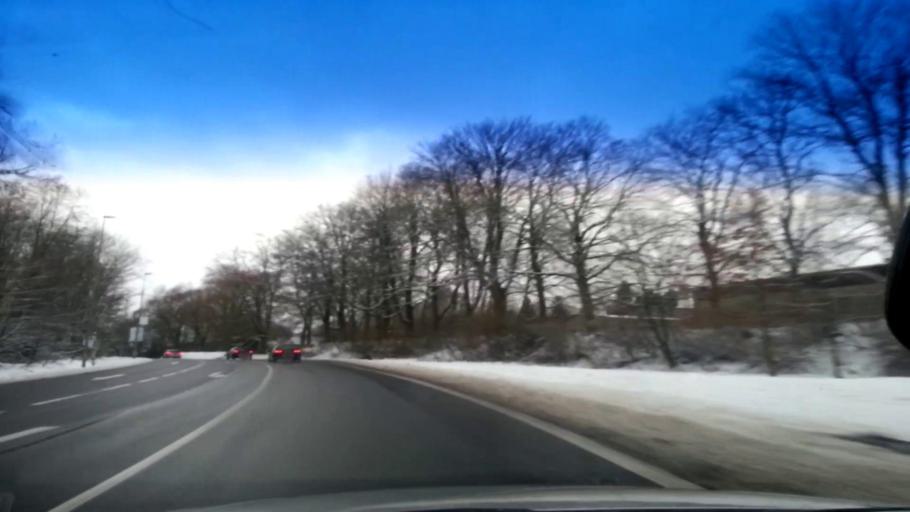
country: CZ
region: Karlovarsky
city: As
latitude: 50.2168
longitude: 12.1750
